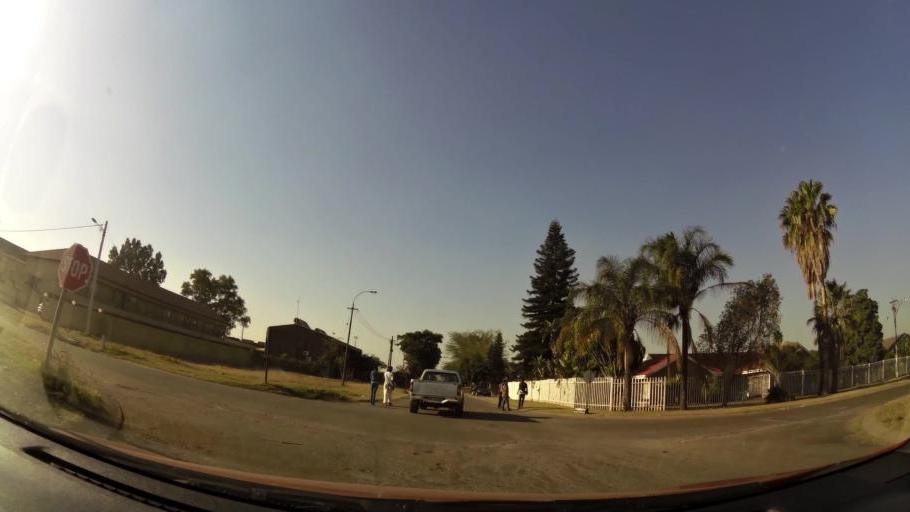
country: ZA
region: North-West
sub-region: Bojanala Platinum District Municipality
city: Rustenburg
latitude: -25.6492
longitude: 27.2423
